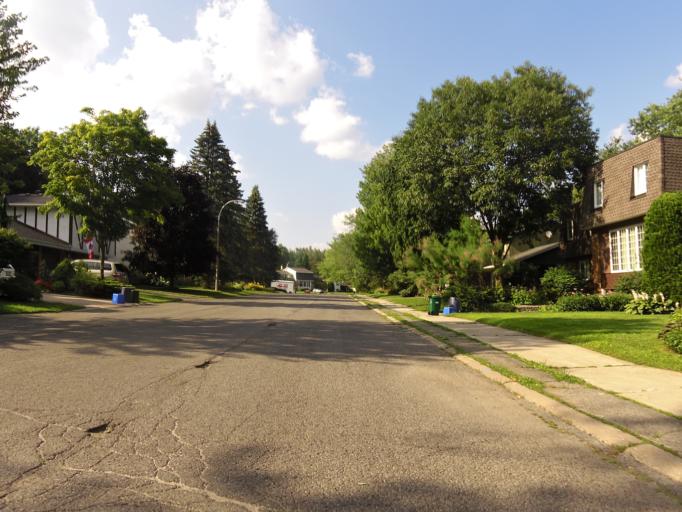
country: CA
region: Ontario
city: Bells Corners
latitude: 45.3201
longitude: -75.7879
